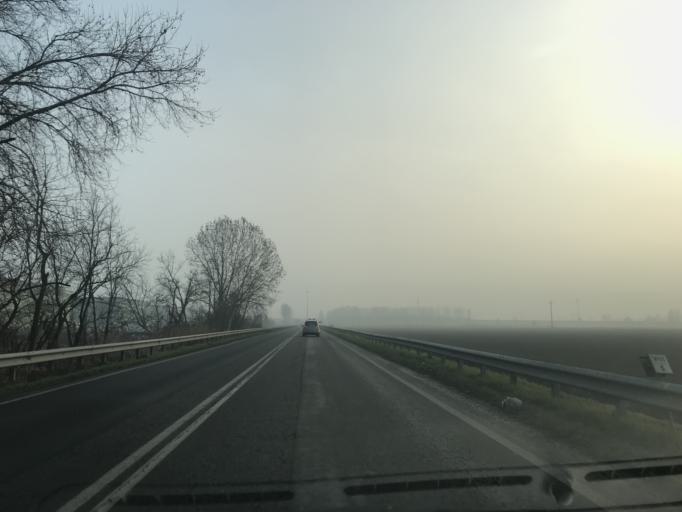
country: IT
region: Lombardy
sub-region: Provincia di Lodi
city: Massalengo-Motta Vigana
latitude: 45.2469
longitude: 9.5012
